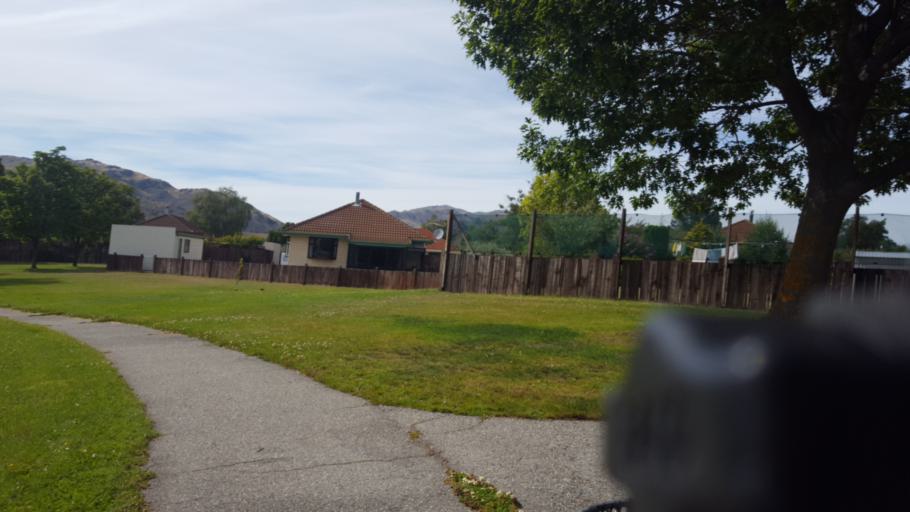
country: NZ
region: Otago
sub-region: Queenstown-Lakes District
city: Wanaka
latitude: -45.0407
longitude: 169.1907
